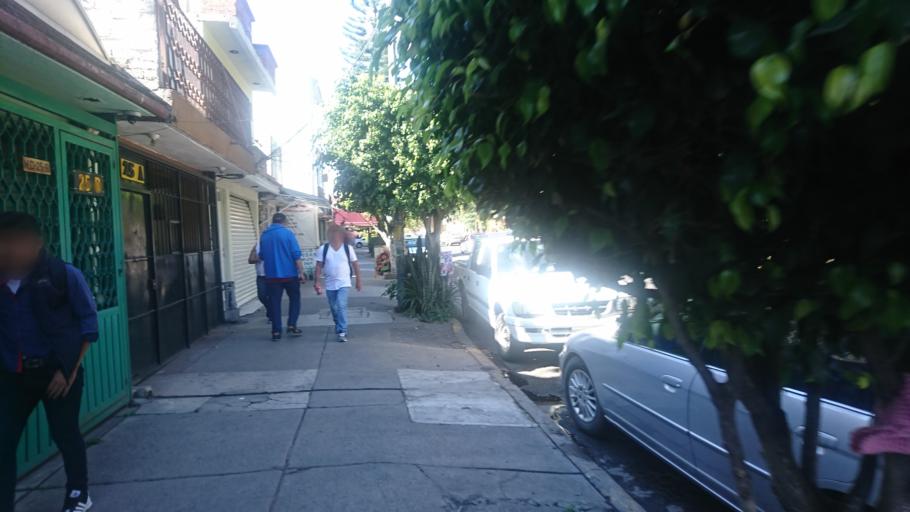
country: MX
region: Mexico City
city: Iztapalapa
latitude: 19.3242
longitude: -99.1058
